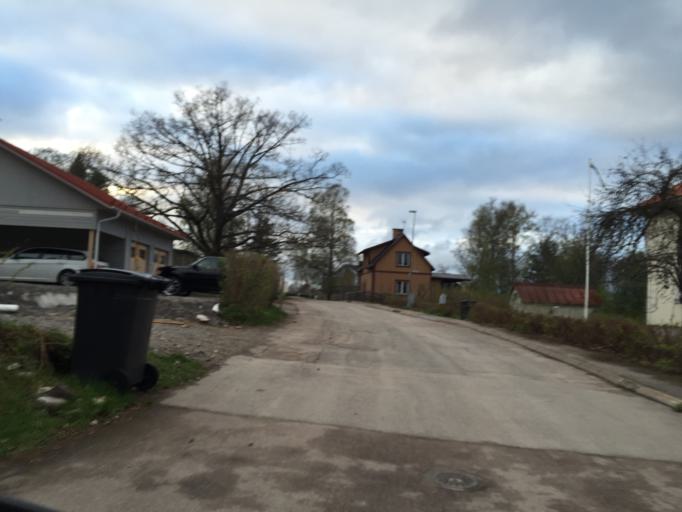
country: SE
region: Dalarna
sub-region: Ludvika Kommun
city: Ludvika
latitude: 60.1396
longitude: 15.1994
